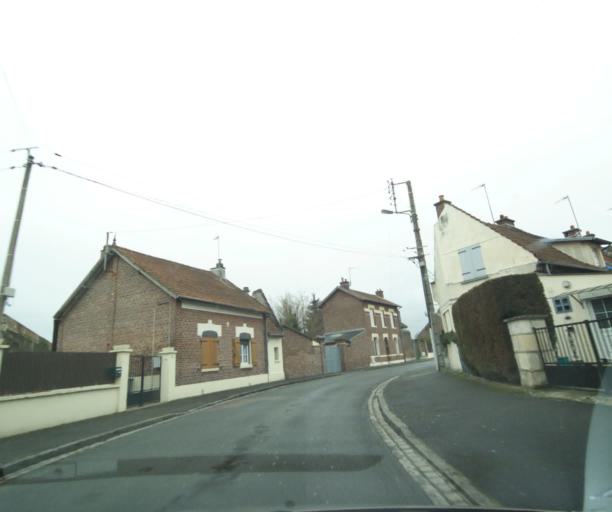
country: FR
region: Picardie
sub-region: Departement de l'Oise
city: Noyon
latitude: 49.5758
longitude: 2.9973
